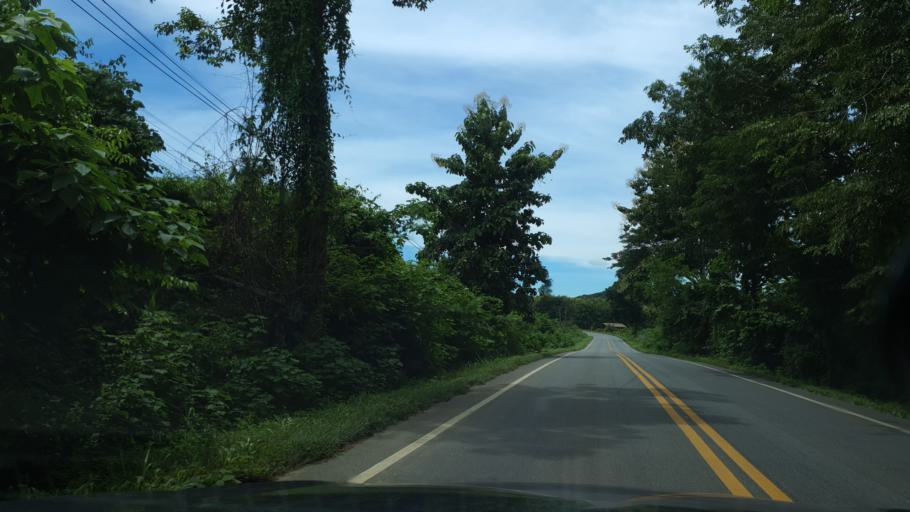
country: TH
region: Sukhothai
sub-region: Amphoe Si Satchanalai
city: Si Satchanalai
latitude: 17.6435
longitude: 99.6860
